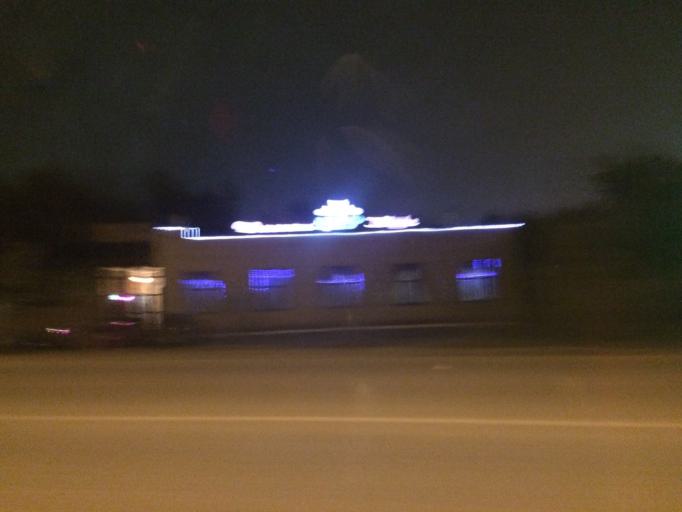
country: KZ
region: Astana Qalasy
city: Astana
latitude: 51.1918
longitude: 71.4613
